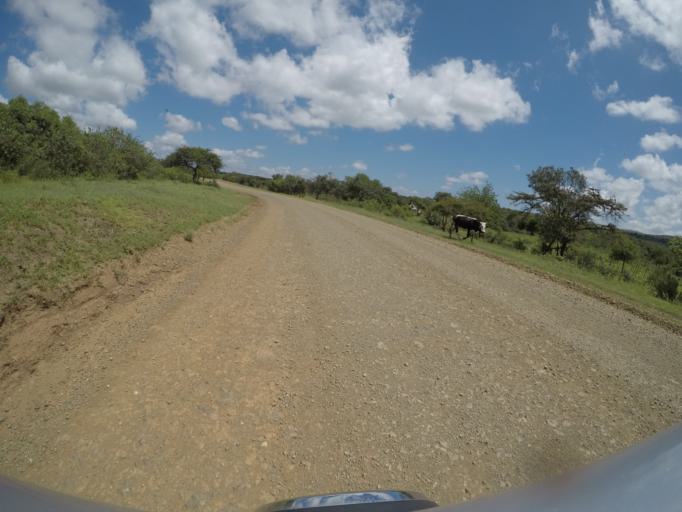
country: ZA
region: KwaZulu-Natal
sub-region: uThungulu District Municipality
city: Empangeni
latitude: -28.5957
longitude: 31.8301
